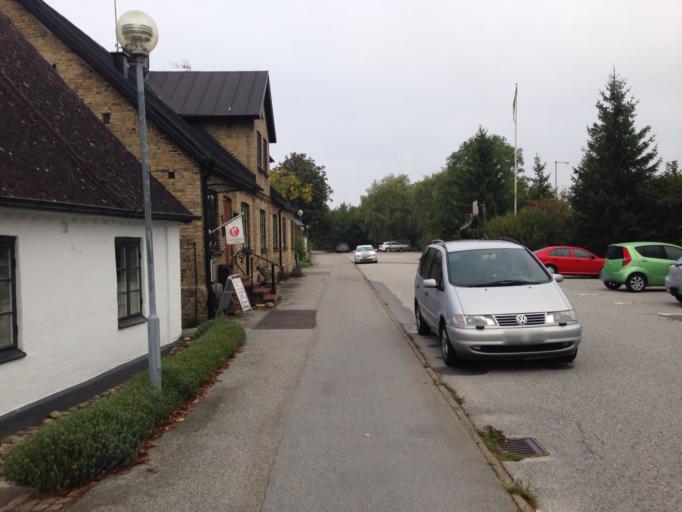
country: SE
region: Skane
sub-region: Lomma Kommun
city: Lomma
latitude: 55.6796
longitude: 13.0719
